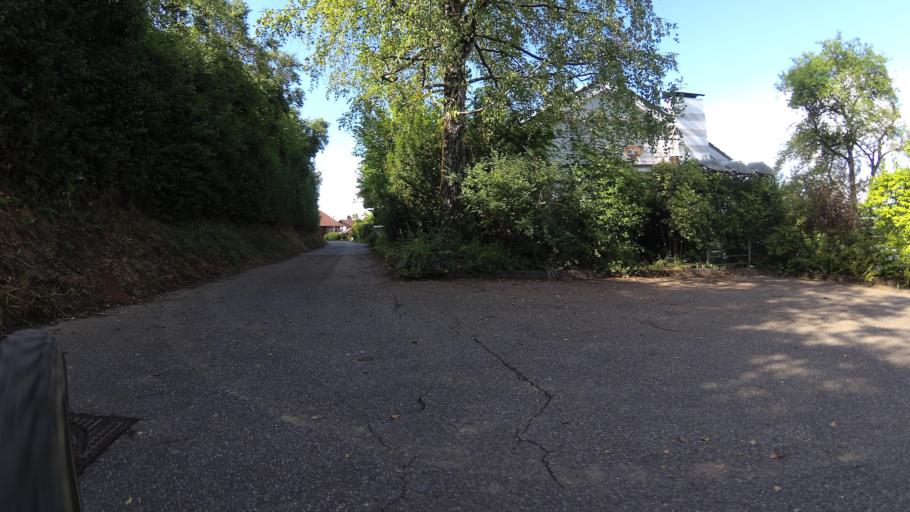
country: DE
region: Baden-Wuerttemberg
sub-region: Regierungsbezirk Stuttgart
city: Neuenstadt am Kocher
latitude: 49.2318
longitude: 9.3255
